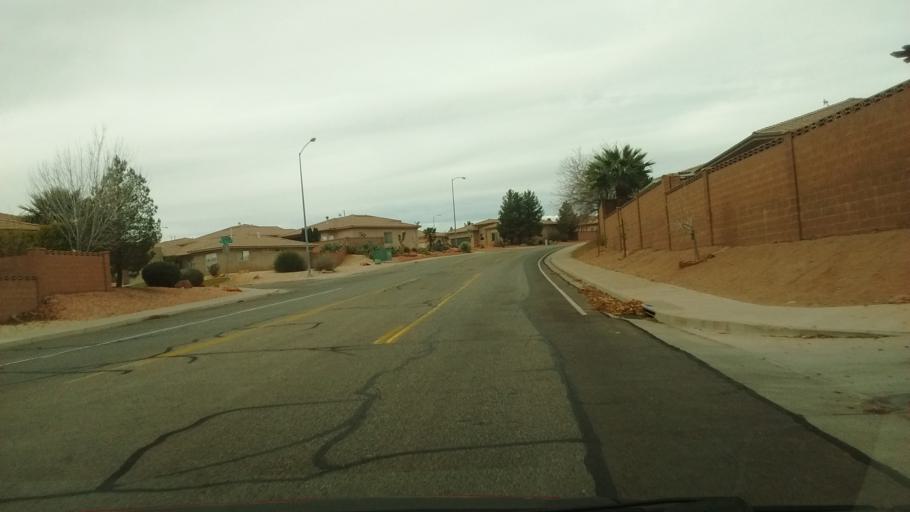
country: US
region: Utah
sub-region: Washington County
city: Washington
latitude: 37.1050
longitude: -113.5310
